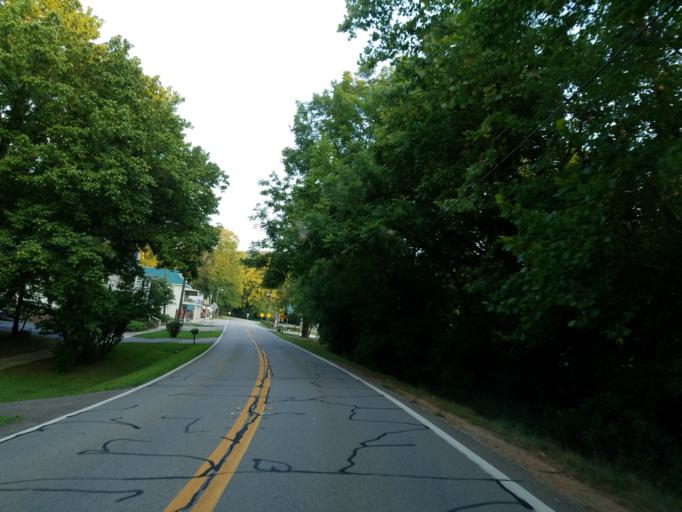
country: US
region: Georgia
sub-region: Pickens County
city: Jasper
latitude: 34.5109
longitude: -84.5068
